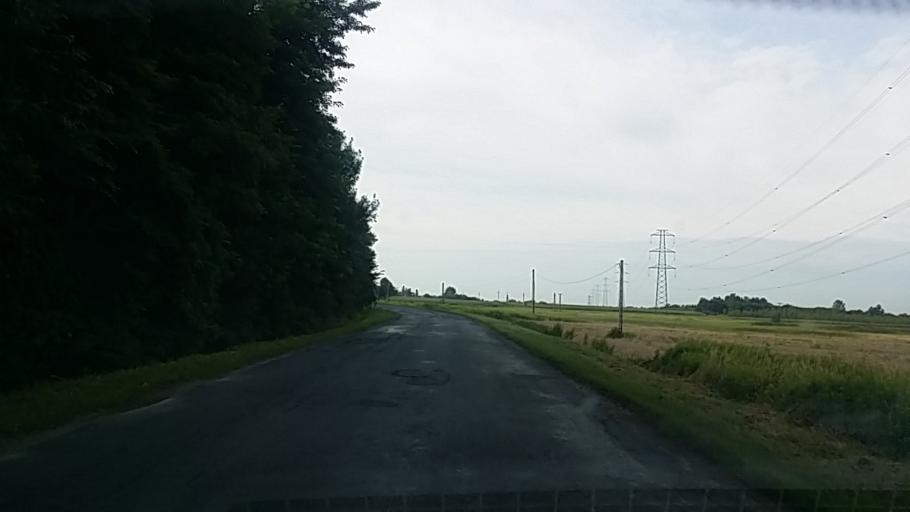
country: HU
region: Zala
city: Lenti
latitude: 46.5509
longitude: 16.5911
